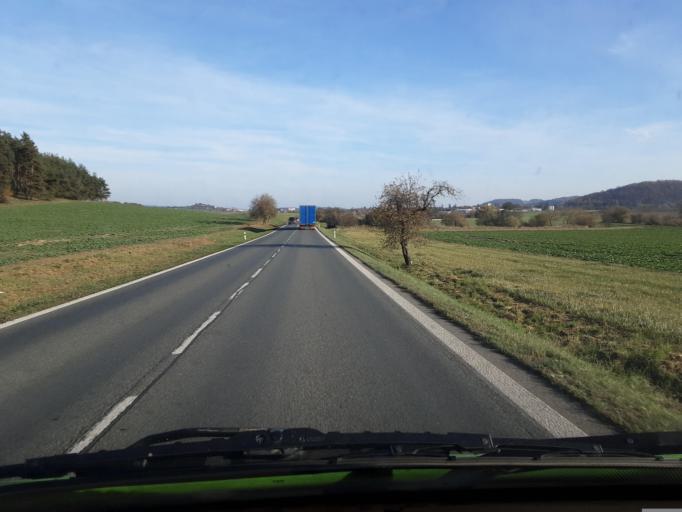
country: CZ
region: Plzensky
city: Horazd'ovice
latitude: 49.3297
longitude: 13.6616
